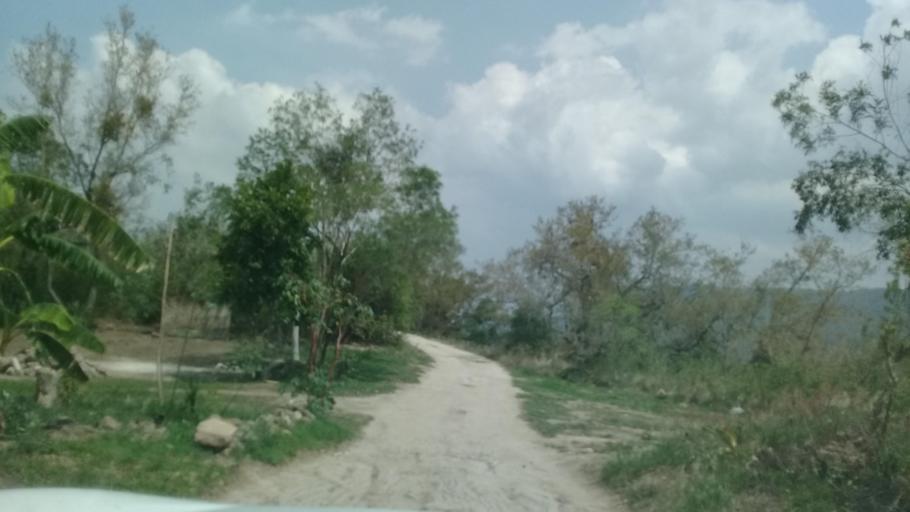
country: MX
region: Veracruz
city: Jalcomulco
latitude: 19.3864
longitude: -96.7912
